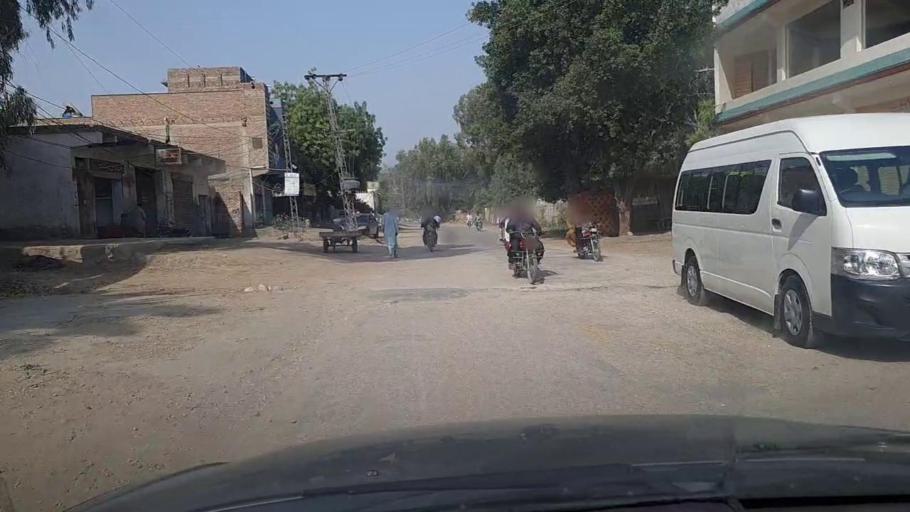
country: PK
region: Sindh
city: Mirpur Mathelo
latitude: 28.0252
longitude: 69.5665
